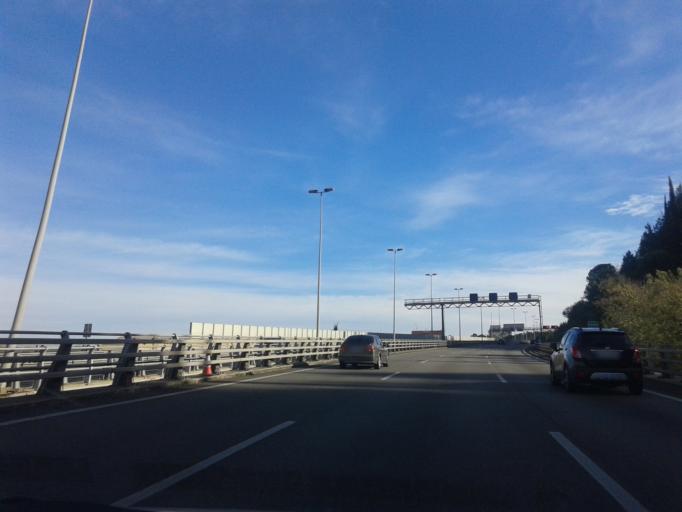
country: ES
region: Catalonia
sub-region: Provincia de Barcelona
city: Martorell
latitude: 41.4710
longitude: 1.9254
